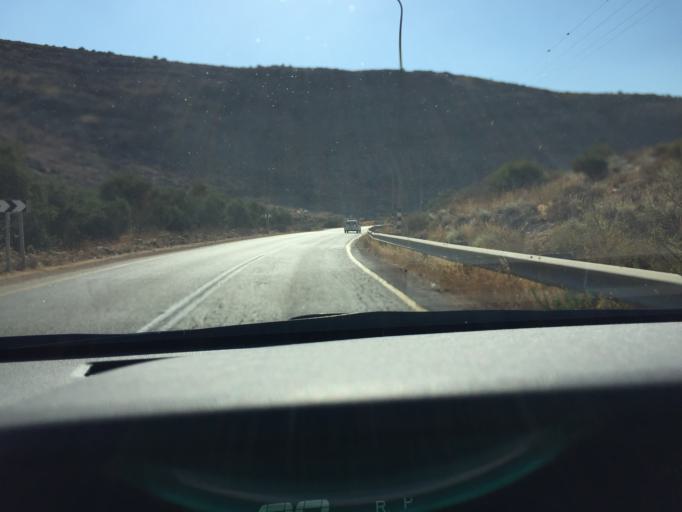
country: PS
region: West Bank
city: Al Lubban al Gharbi
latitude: 32.0487
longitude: 35.0435
